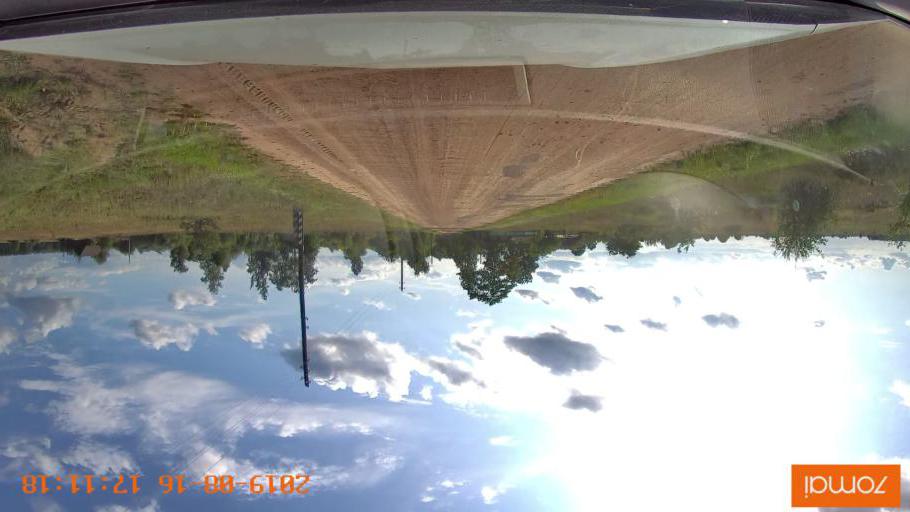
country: BY
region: Mogilev
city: Hlusha
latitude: 53.1954
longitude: 28.9080
